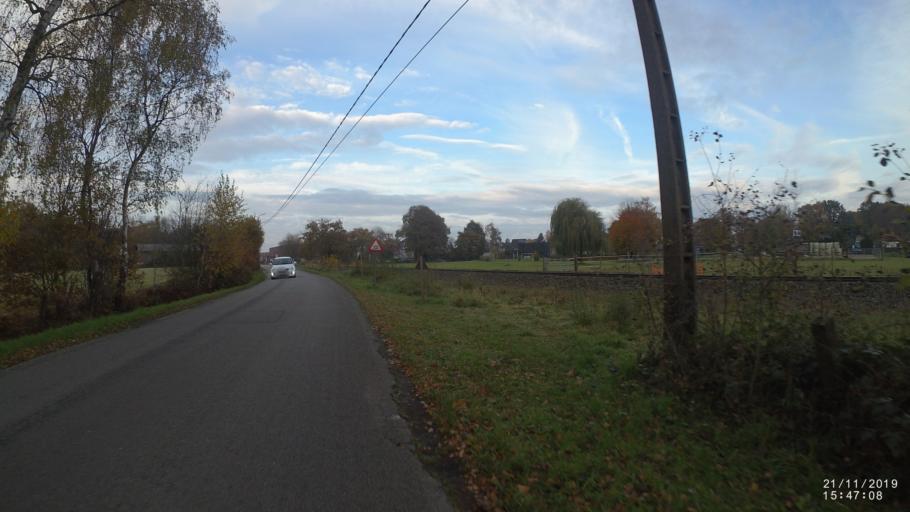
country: BE
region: Flanders
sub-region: Provincie Limburg
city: Zonhoven
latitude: 50.9781
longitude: 5.3476
